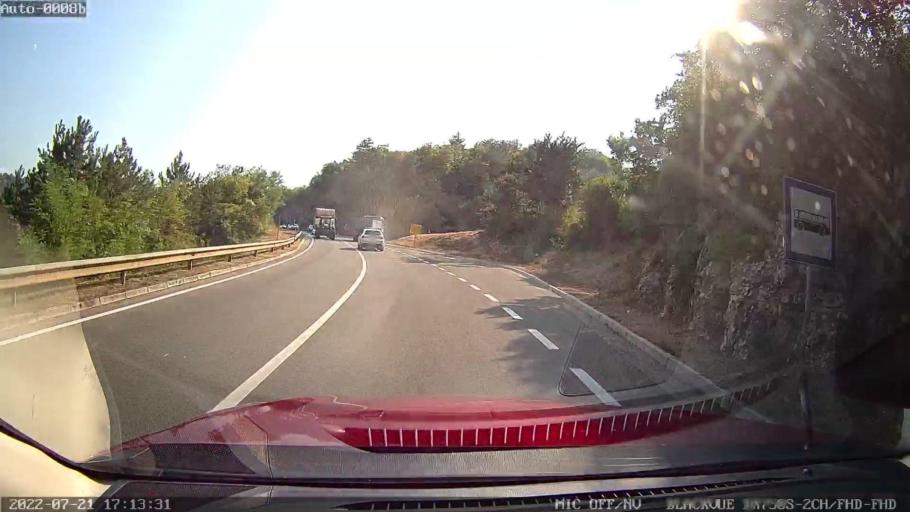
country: HR
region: Istarska
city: Pazin
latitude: 45.2502
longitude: 13.8818
